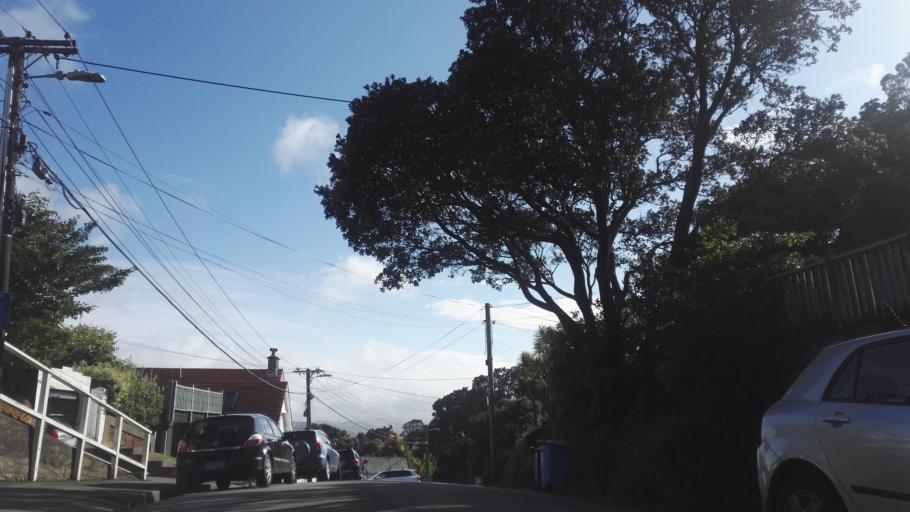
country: NZ
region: Wellington
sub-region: Wellington City
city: Kelburn
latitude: -41.2900
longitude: 174.7639
